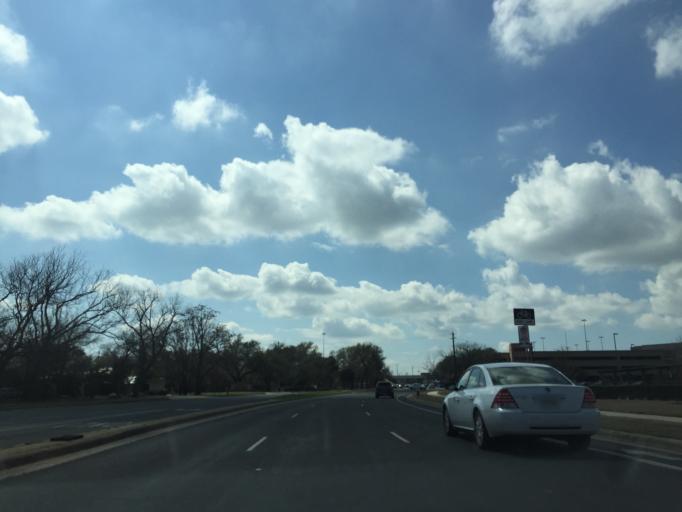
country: US
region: Texas
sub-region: Williamson County
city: Anderson Mill
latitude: 30.4639
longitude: -97.7893
